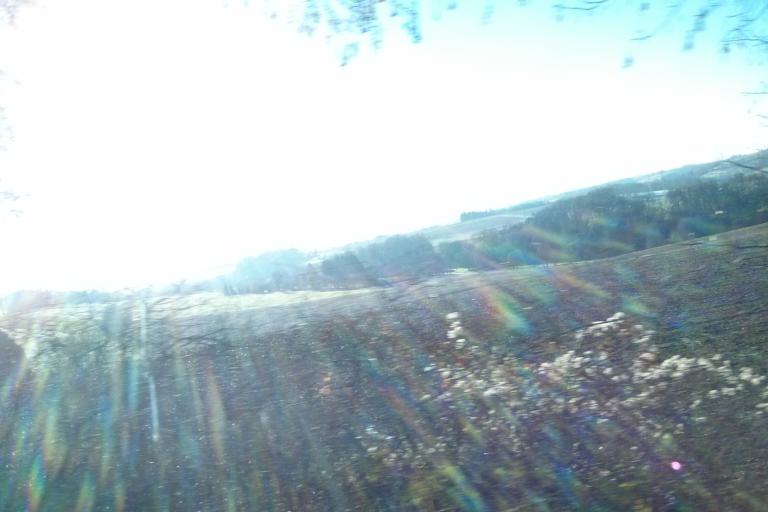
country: DE
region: North Rhine-Westphalia
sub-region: Regierungsbezirk Koln
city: Hennef
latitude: 50.7627
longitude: 7.3268
